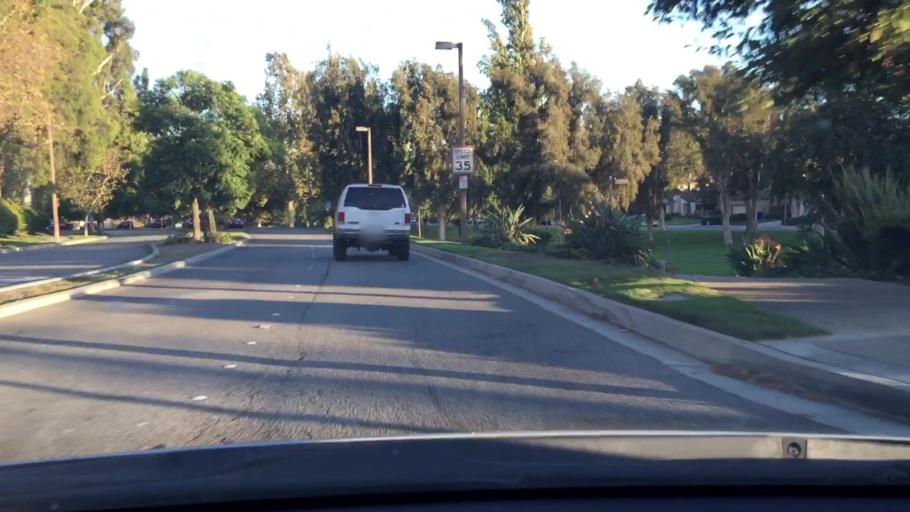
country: US
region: California
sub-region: Los Angeles County
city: Pomona
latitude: 34.0290
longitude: -117.7748
